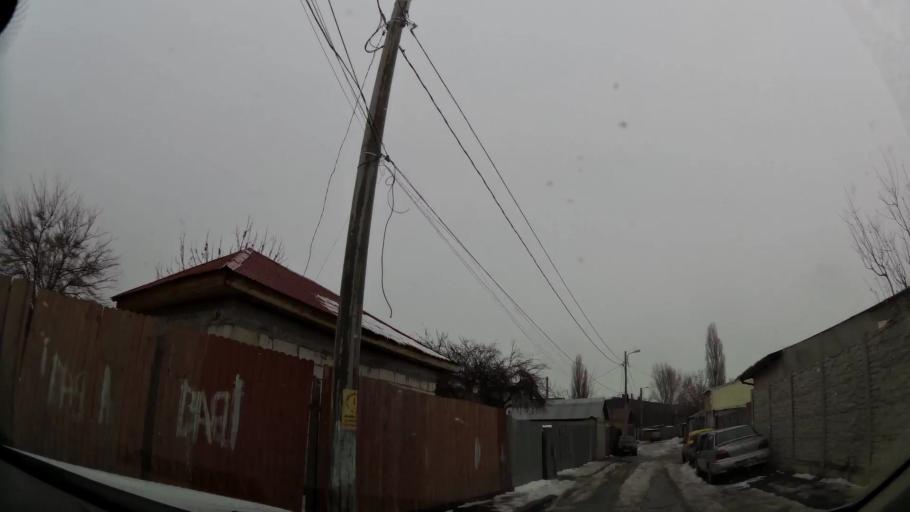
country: RO
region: Ilfov
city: Dobroesti
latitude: 44.4220
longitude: 26.1849
